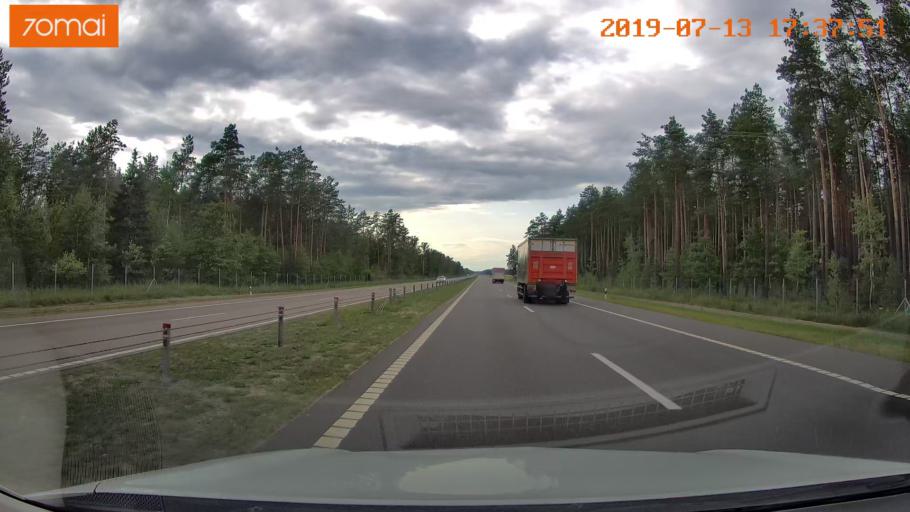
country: BY
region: Mogilev
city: Yalizava
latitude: 53.2620
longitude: 28.8947
